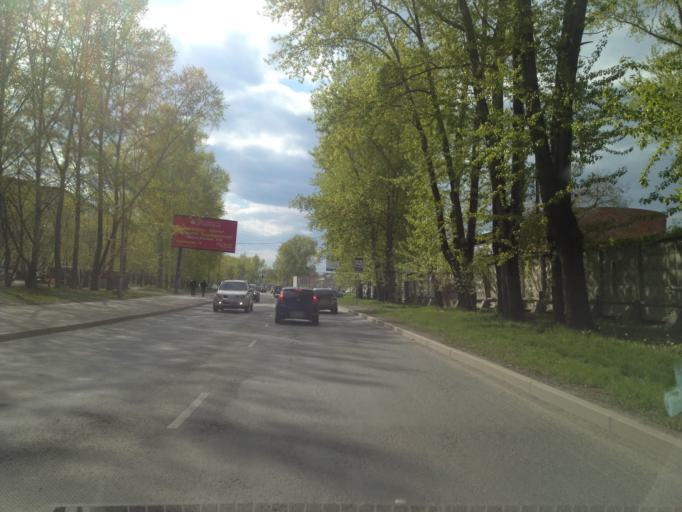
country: RU
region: Sverdlovsk
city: Yekaterinburg
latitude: 56.8574
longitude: 60.5687
